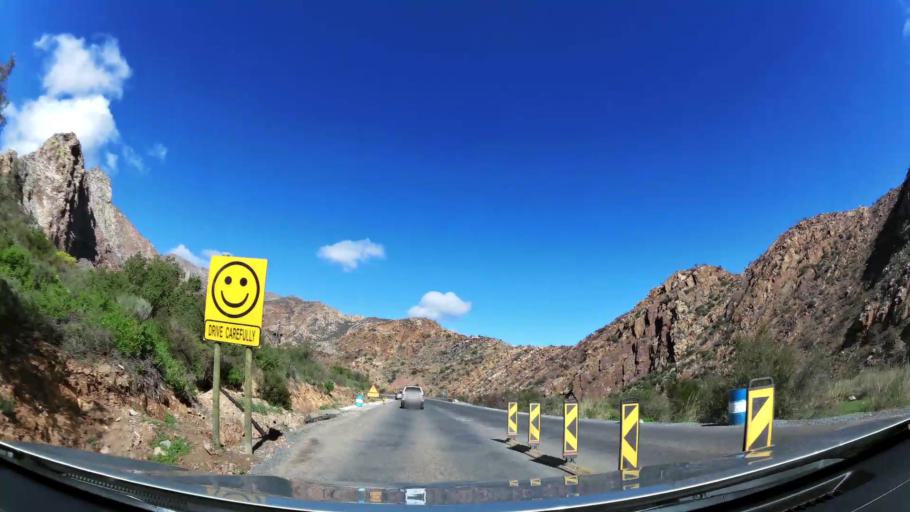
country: ZA
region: Western Cape
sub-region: Cape Winelands District Municipality
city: Ashton
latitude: -33.7954
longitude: 20.1035
